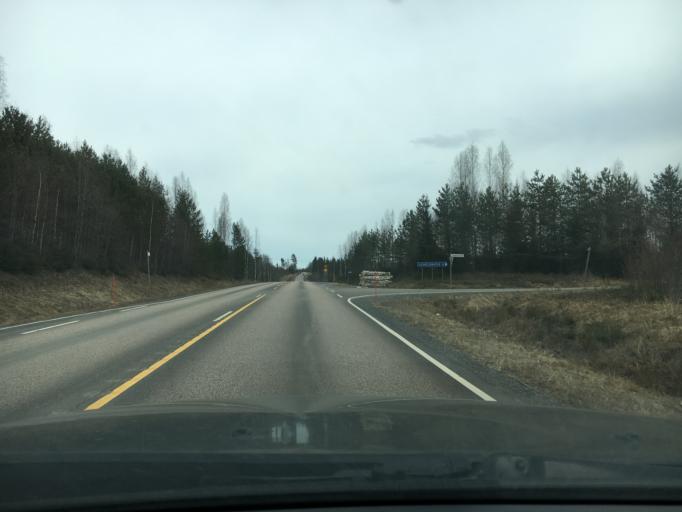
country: FI
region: Central Finland
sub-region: AEaenekoski
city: Konnevesi
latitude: 62.6928
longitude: 26.4193
